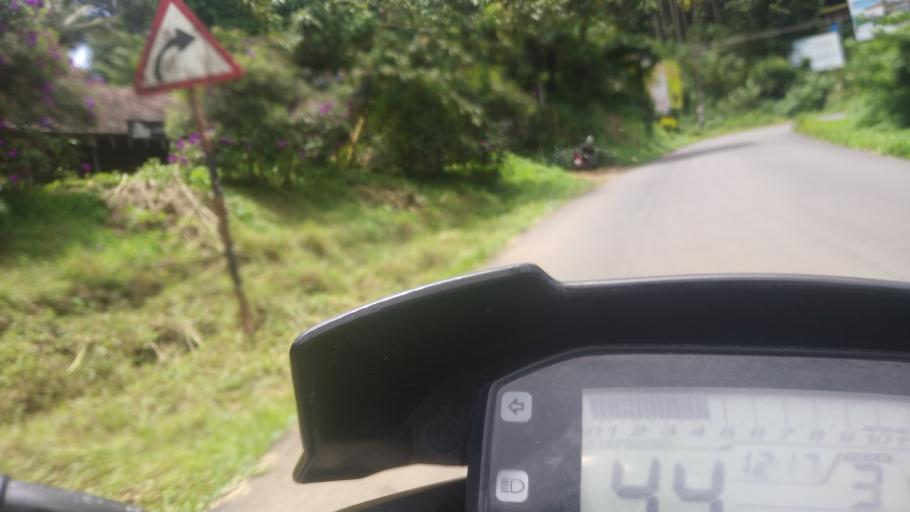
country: IN
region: Kerala
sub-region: Idukki
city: Munnar
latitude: 10.0181
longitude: 77.0113
